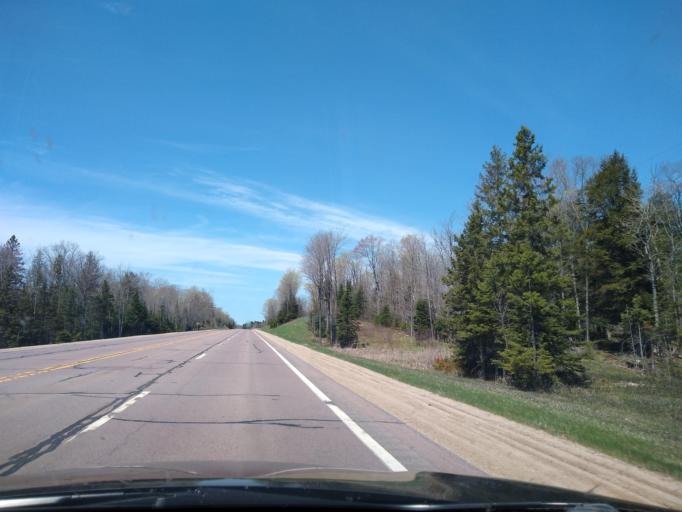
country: US
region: Michigan
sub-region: Marquette County
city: K. I. Sawyer Air Force Base
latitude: 46.2611
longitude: -87.0968
